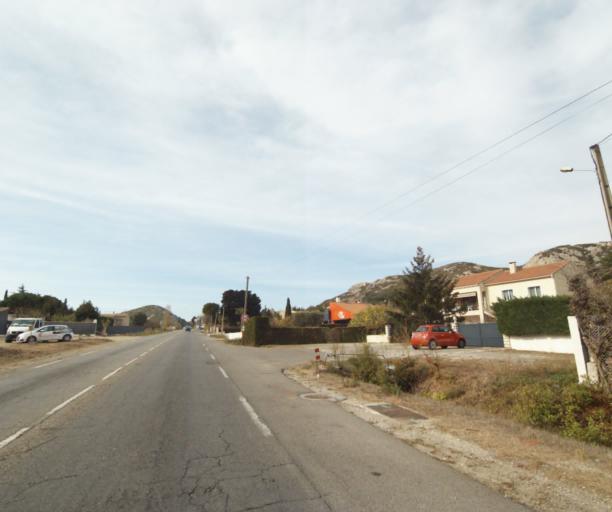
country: FR
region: Provence-Alpes-Cote d'Azur
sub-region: Departement des Bouches-du-Rhone
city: Le Rove
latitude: 43.3673
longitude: 5.2472
